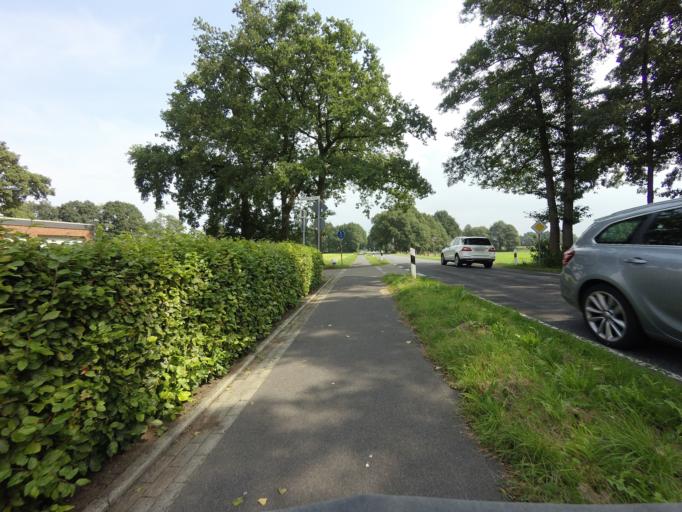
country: DE
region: Lower Saxony
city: Lage
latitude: 52.4743
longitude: 6.9490
